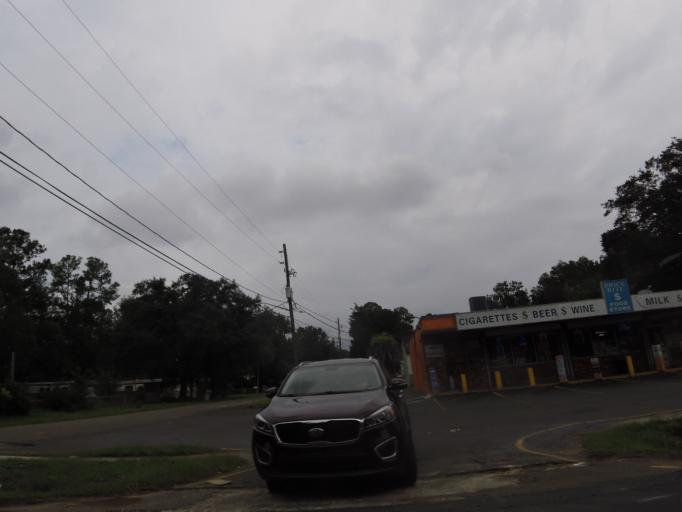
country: US
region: Florida
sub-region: Clay County
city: Bellair-Meadowbrook Terrace
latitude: 30.2338
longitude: -81.7195
